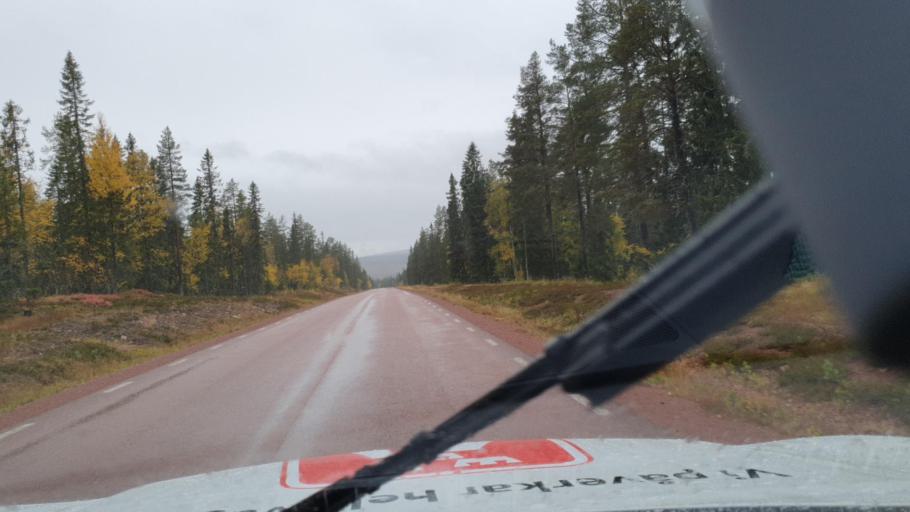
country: SE
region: Dalarna
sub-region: Alvdalens Kommun
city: AElvdalen
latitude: 61.4509
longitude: 14.1609
